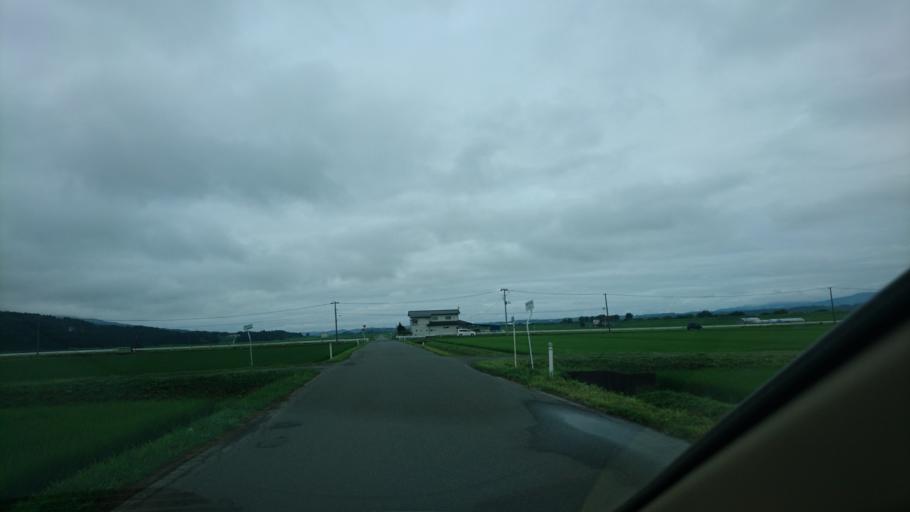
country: JP
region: Iwate
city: Mizusawa
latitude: 39.0619
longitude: 141.1710
